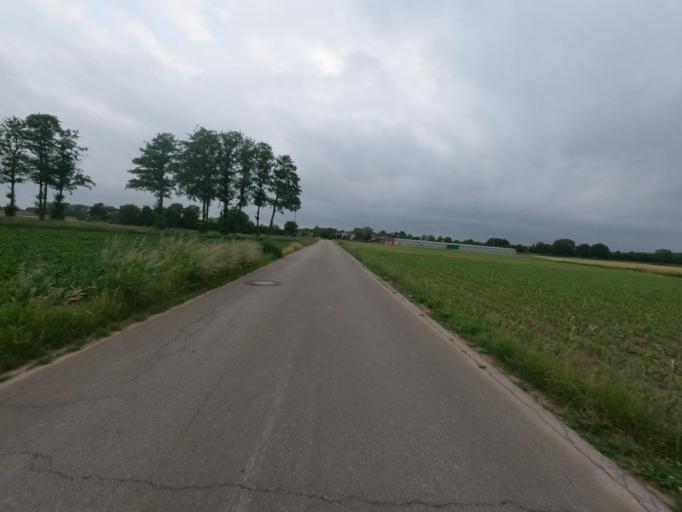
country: DE
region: North Rhine-Westphalia
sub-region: Regierungsbezirk Koln
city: Wassenberg
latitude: 51.0923
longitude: 6.1454
